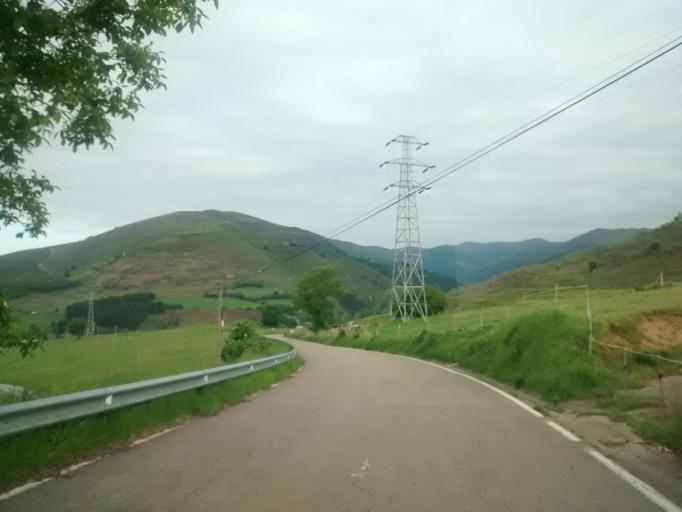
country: ES
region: Cantabria
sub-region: Provincia de Cantabria
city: San Vicente de la Barquera
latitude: 43.2526
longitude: -4.4239
